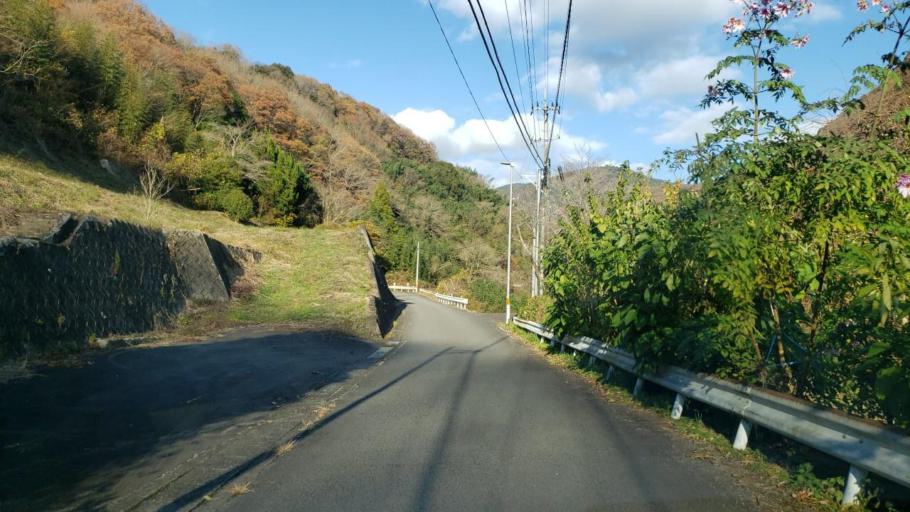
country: JP
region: Tokushima
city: Wakimachi
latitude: 34.0973
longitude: 134.0685
